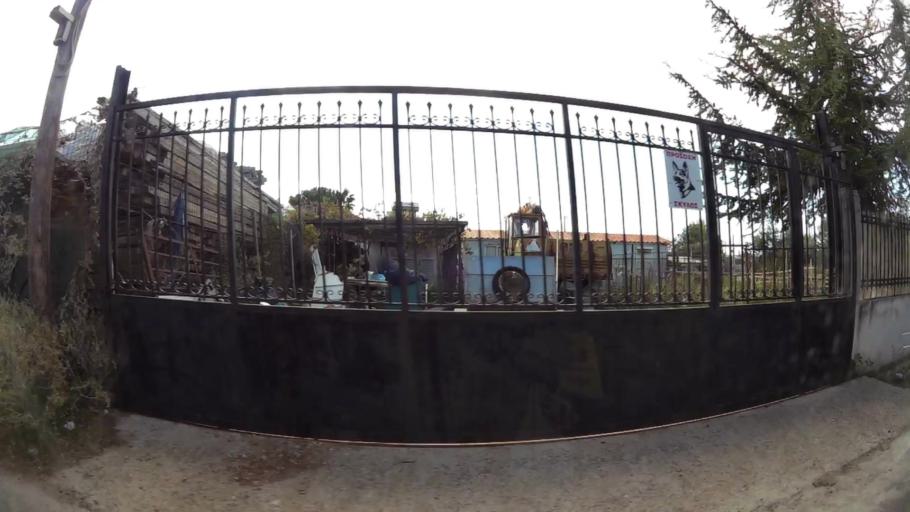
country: GR
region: Attica
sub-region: Nomarchia Anatolikis Attikis
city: Thrakomakedones
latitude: 38.1069
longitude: 23.7613
